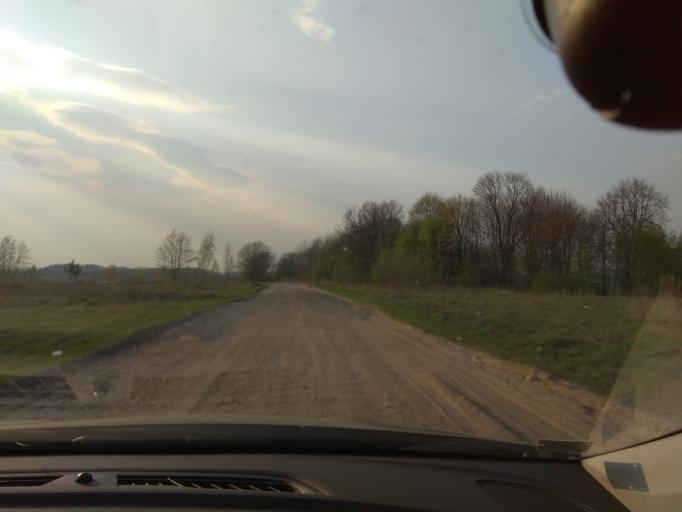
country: LT
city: Baltoji Voke
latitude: 54.5932
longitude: 25.1689
